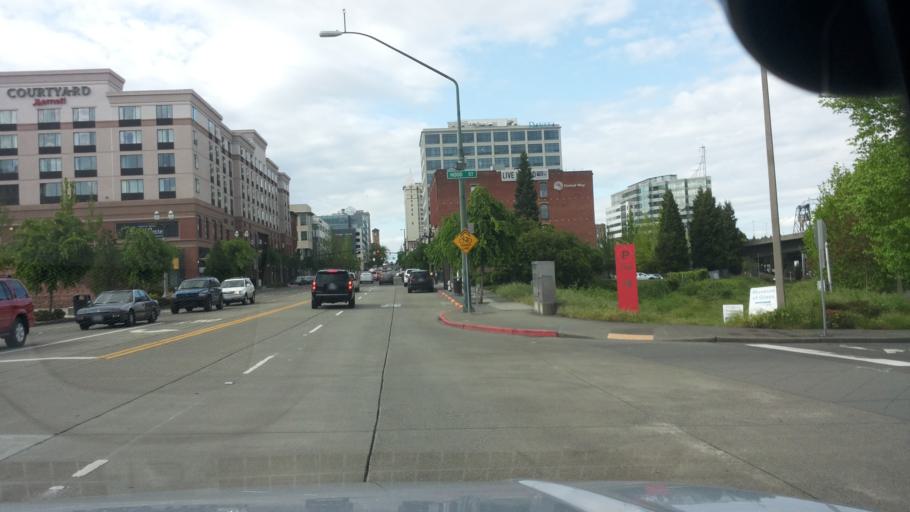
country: US
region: Washington
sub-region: Pierce County
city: Tacoma
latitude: 47.2475
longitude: -122.4372
